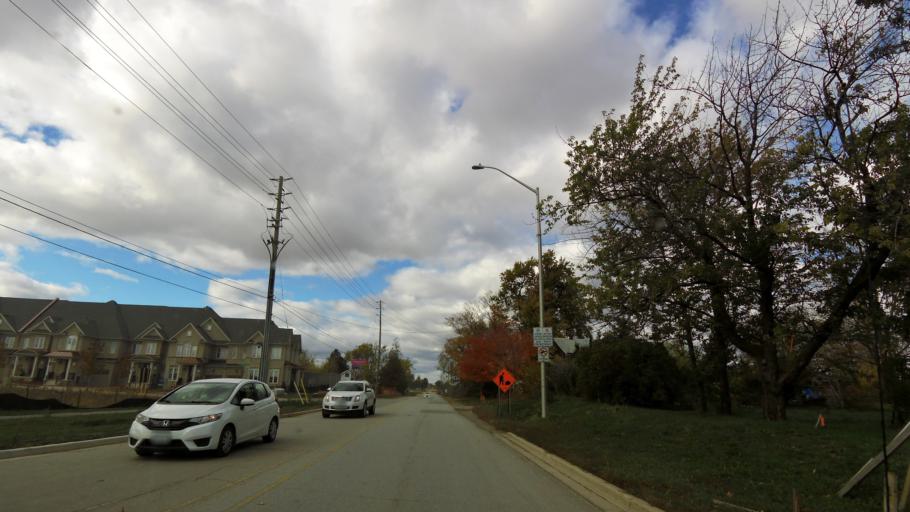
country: CA
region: Ontario
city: Oakville
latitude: 43.4801
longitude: -79.7304
